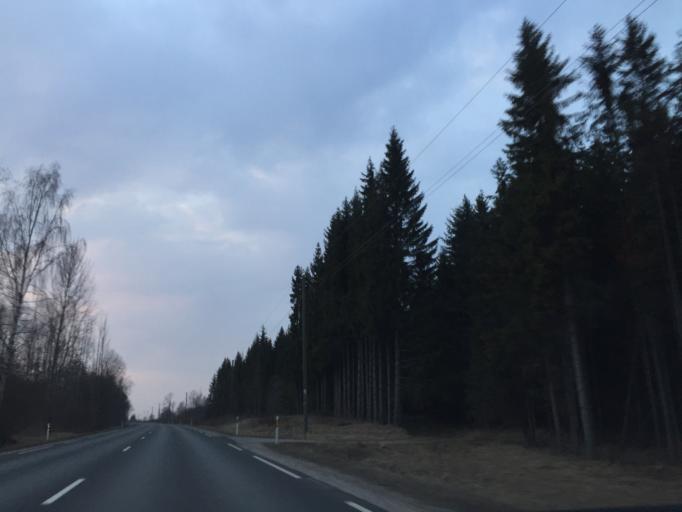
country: LV
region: Raunas
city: Rauna
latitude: 57.2365
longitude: 25.5658
